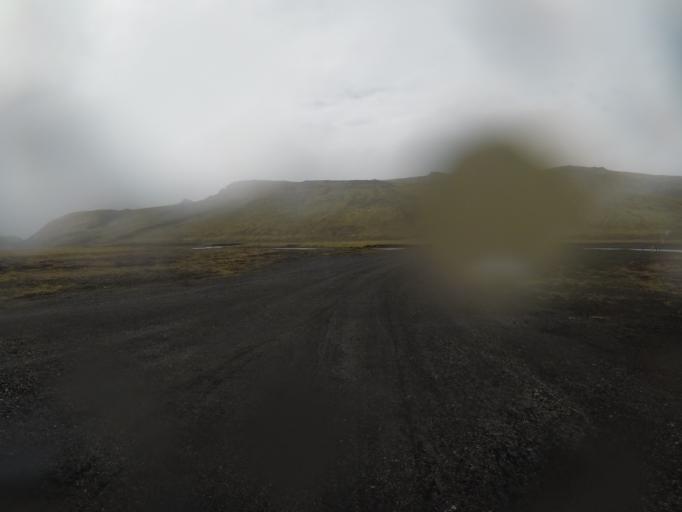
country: IS
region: South
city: Vestmannaeyjar
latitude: 63.9747
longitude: -18.8442
